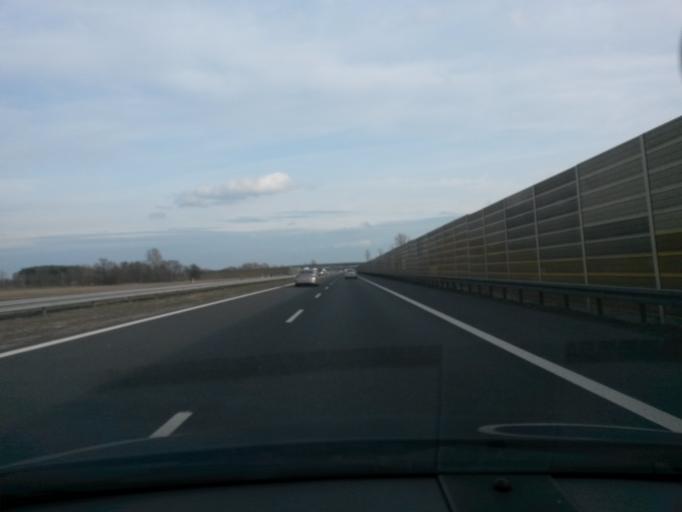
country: PL
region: Greater Poland Voivodeship
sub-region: Powiat kolski
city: Dabie
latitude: 52.0513
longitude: 18.8468
